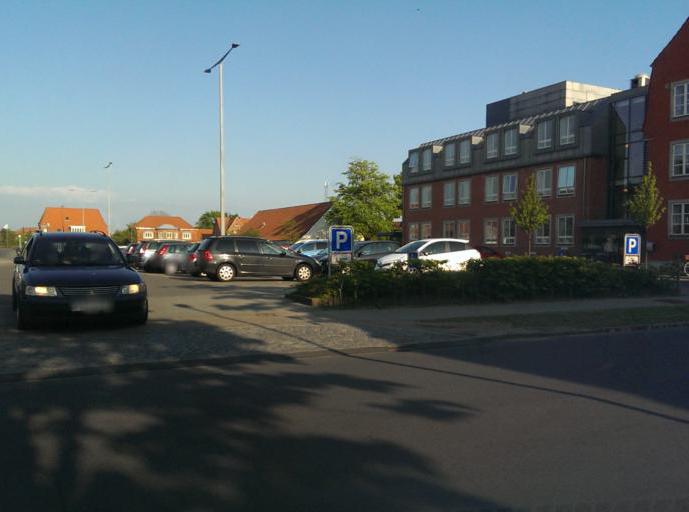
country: DK
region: South Denmark
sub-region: Esbjerg Kommune
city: Esbjerg
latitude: 55.4725
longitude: 8.4561
